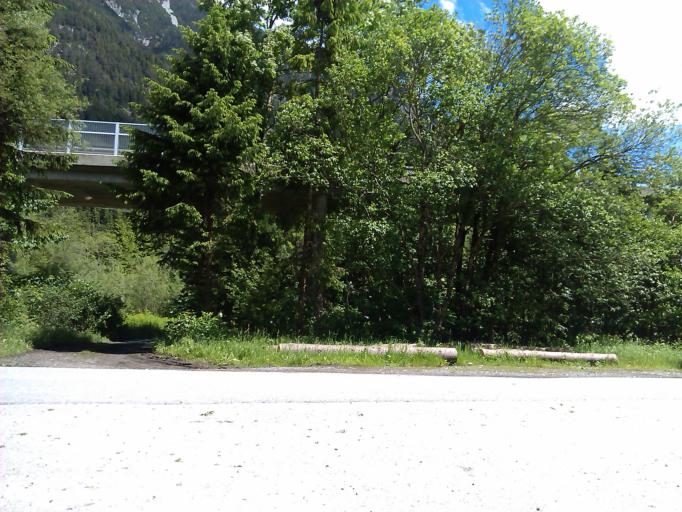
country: AT
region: Tyrol
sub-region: Politischer Bezirk Reutte
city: Bichlbach
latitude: 47.4282
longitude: 10.7768
